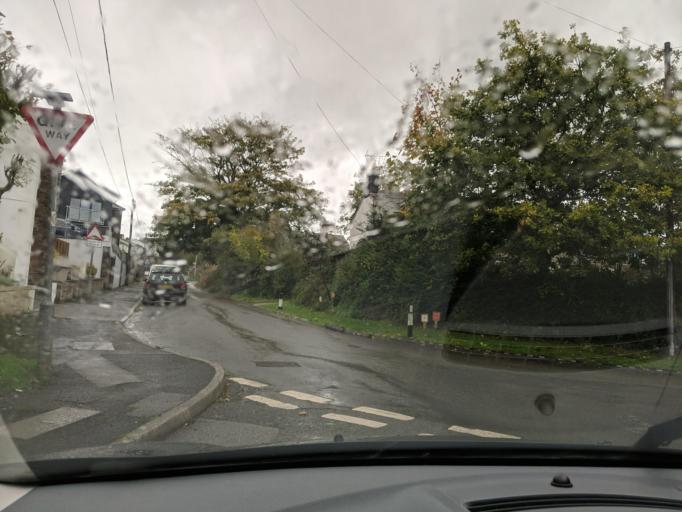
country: GB
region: England
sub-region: Cornwall
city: Wadebridge
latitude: 50.5149
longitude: -4.8213
